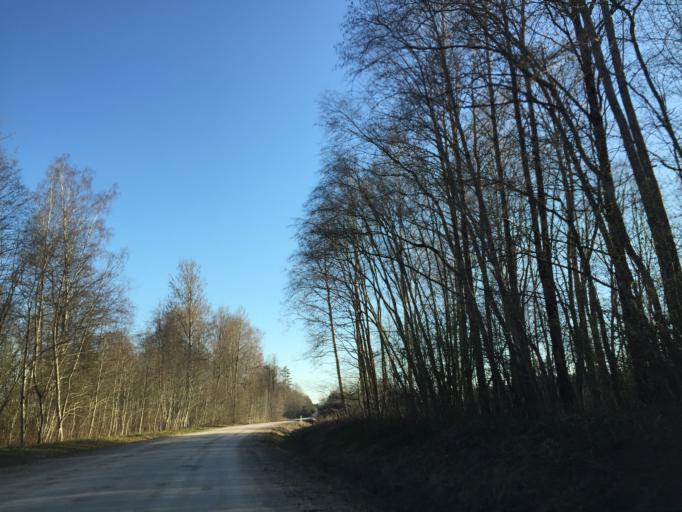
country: RU
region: Leningrad
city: Slantsy
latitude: 59.1003
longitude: 27.7943
